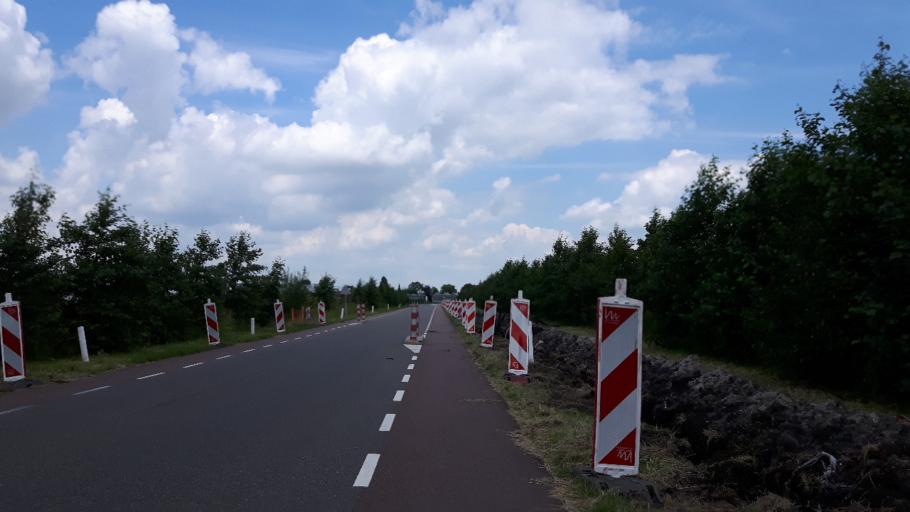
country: NL
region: South Holland
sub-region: Gemeente Boskoop
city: Boskoop
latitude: 52.0678
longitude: 4.6826
